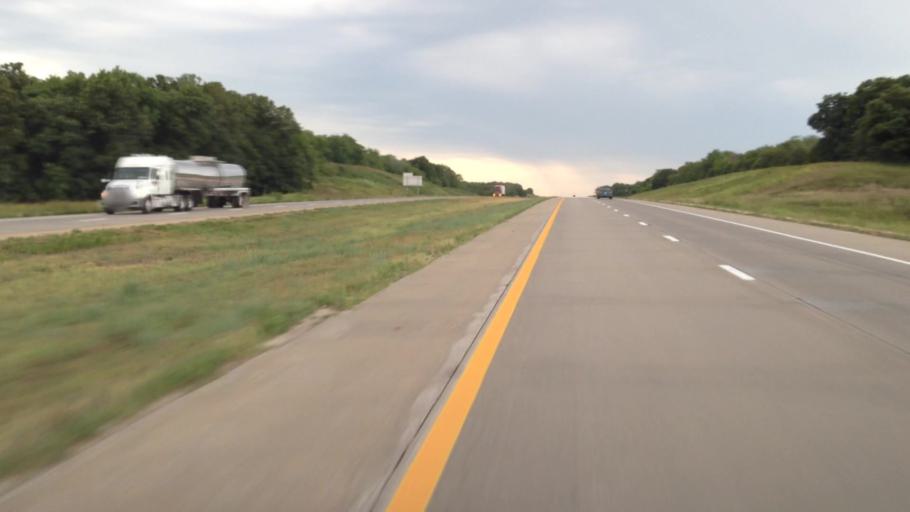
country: US
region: Kansas
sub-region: Osage County
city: Lyndon
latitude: 38.4838
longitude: -95.4938
